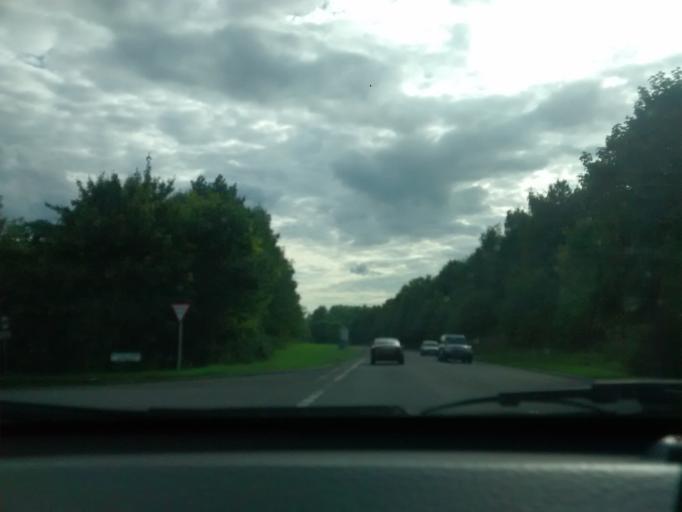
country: GB
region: England
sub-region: Norfolk
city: Downham Market
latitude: 52.5910
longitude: 0.3896
